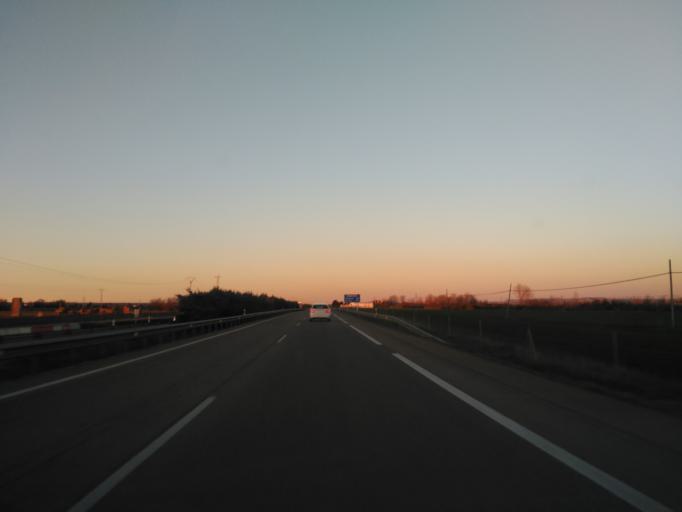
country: ES
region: Castille and Leon
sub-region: Provincia de Valladolid
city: Cabezon
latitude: 41.7600
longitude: -4.6316
